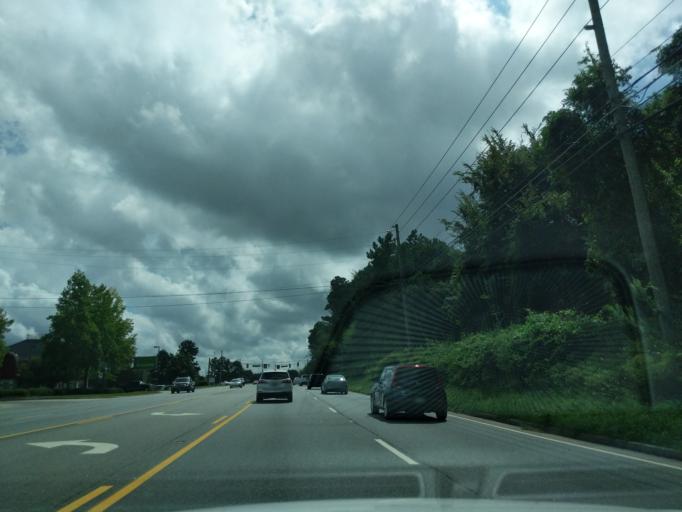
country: US
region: Georgia
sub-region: Columbia County
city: Evans
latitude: 33.5428
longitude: -82.1380
